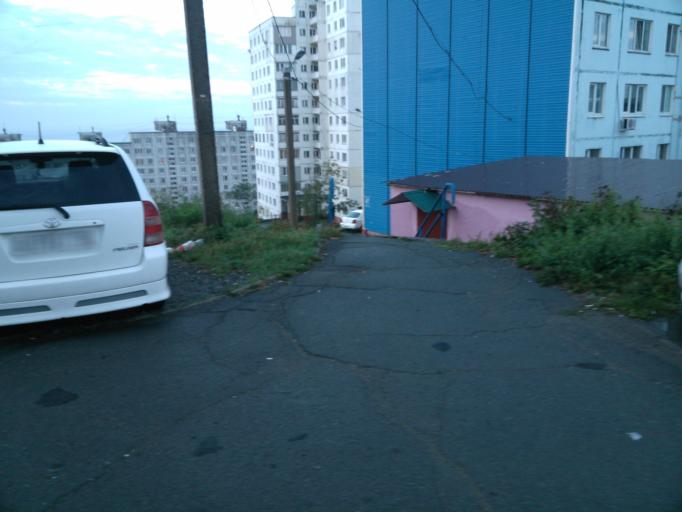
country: RU
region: Primorskiy
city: Vladivostok
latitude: 43.0946
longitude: 131.9740
